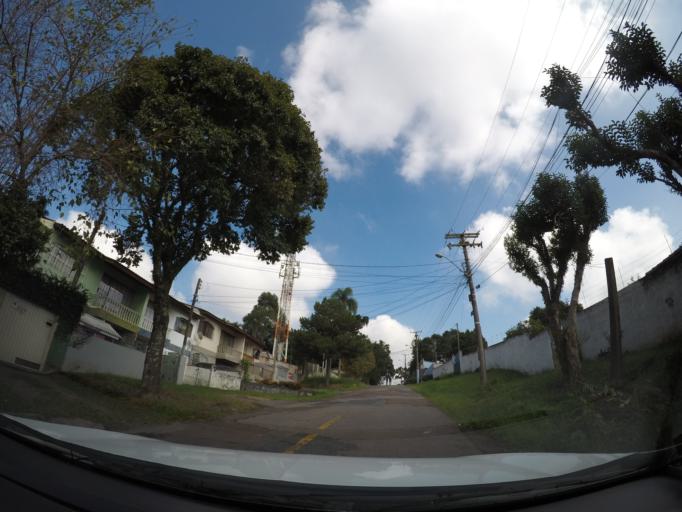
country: BR
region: Parana
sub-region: Sao Jose Dos Pinhais
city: Sao Jose dos Pinhais
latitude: -25.4922
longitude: -49.2153
